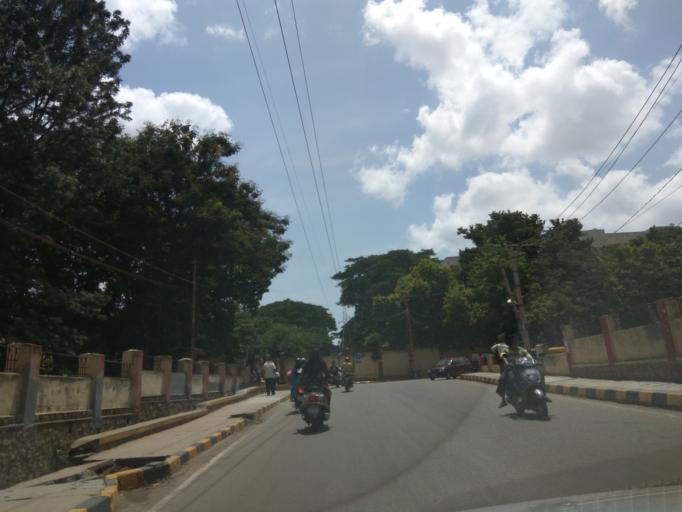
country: IN
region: Karnataka
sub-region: Bangalore Urban
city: Bangalore
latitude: 12.9854
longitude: 77.6641
